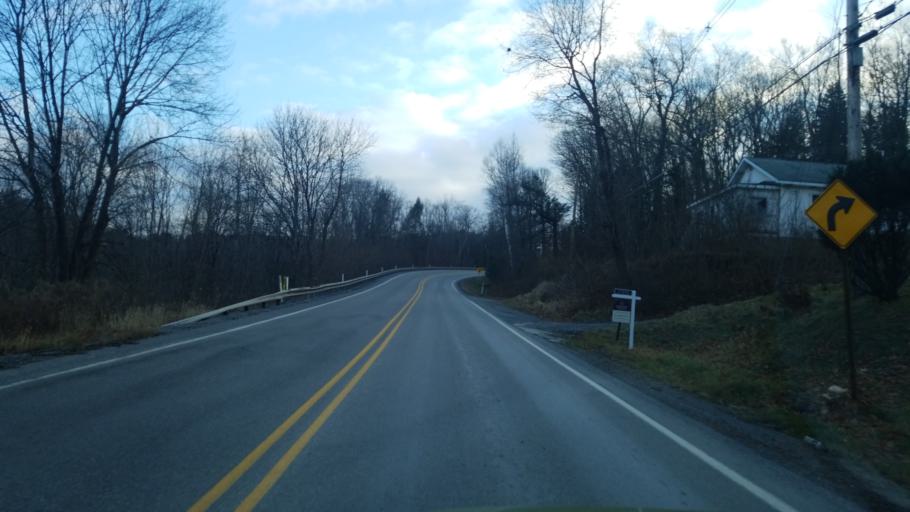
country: US
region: Pennsylvania
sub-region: Clearfield County
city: Clearfield
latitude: 41.0028
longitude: -78.4256
